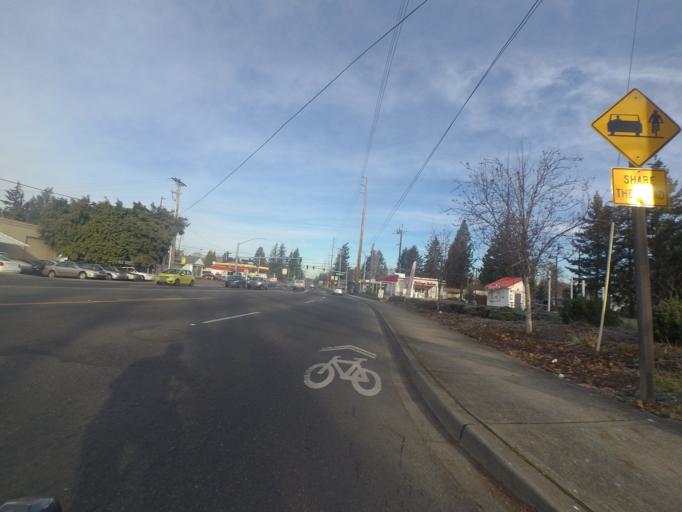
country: US
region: Washington
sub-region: Pierce County
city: Lakewood
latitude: 47.1757
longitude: -122.5181
